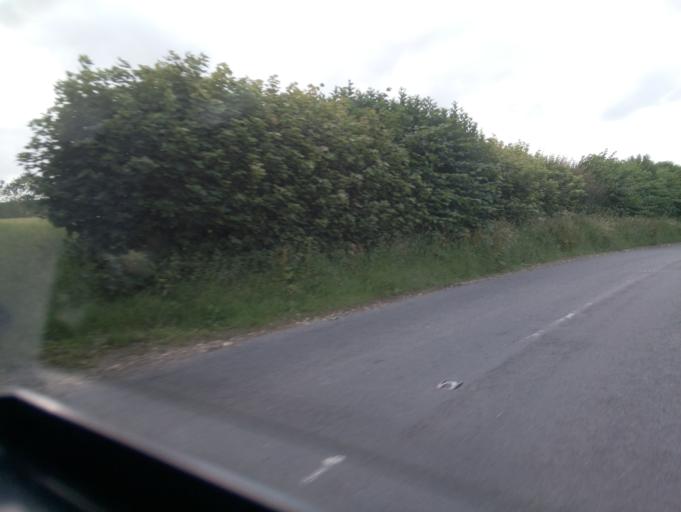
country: GB
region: England
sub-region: Gloucestershire
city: Chipping Campden
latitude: 52.0084
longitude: -1.7618
